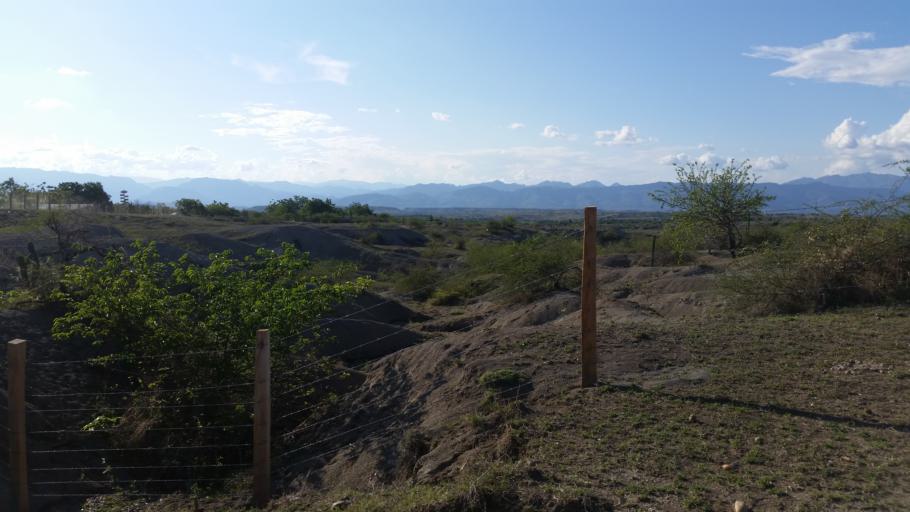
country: CO
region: Huila
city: Villavieja
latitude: 3.2322
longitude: -75.1566
